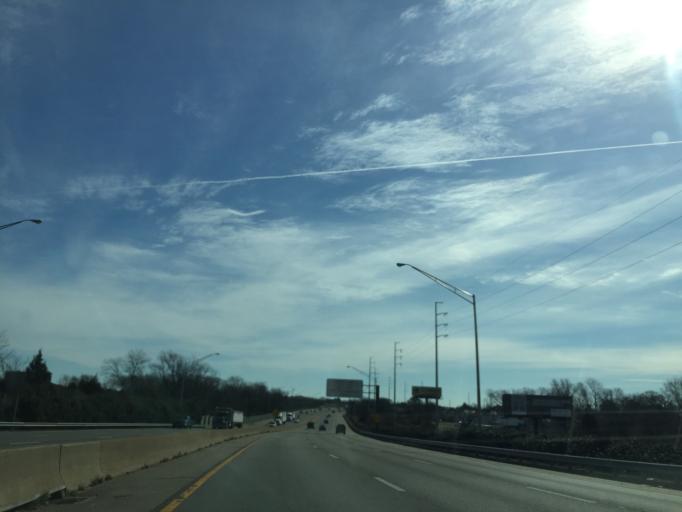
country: US
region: Virginia
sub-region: City of Hampton
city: Hampton
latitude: 37.0341
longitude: -76.3461
